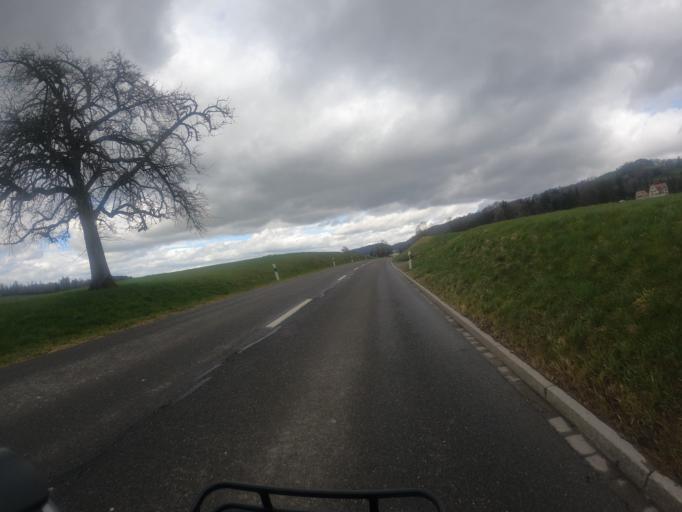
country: CH
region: Zurich
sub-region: Bezirk Affoltern
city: Hausen am Albis / Hausen (Dorf)
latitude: 47.2304
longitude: 8.5465
